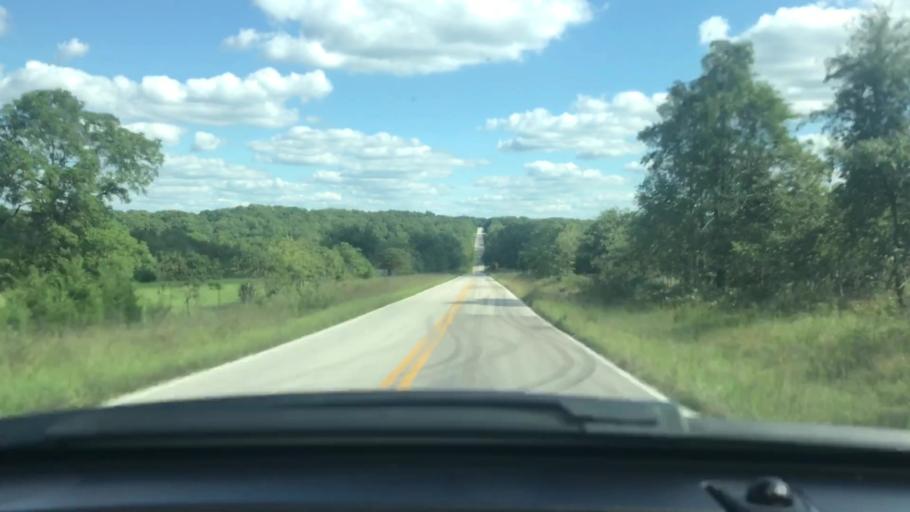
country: US
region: Missouri
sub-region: Wright County
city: Hartville
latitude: 37.3874
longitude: -92.4449
